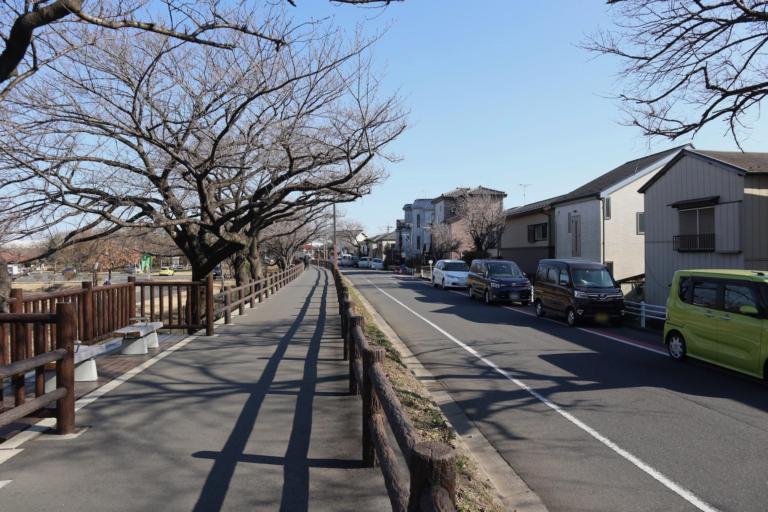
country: JP
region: Chiba
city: Matsudo
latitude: 35.7803
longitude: 139.8763
